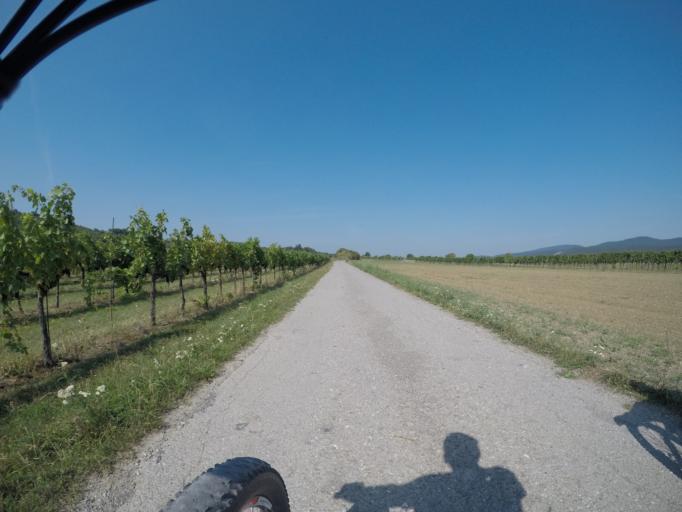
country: AT
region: Lower Austria
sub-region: Politischer Bezirk Baden
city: Hirtenberg
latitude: 47.9505
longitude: 16.1789
